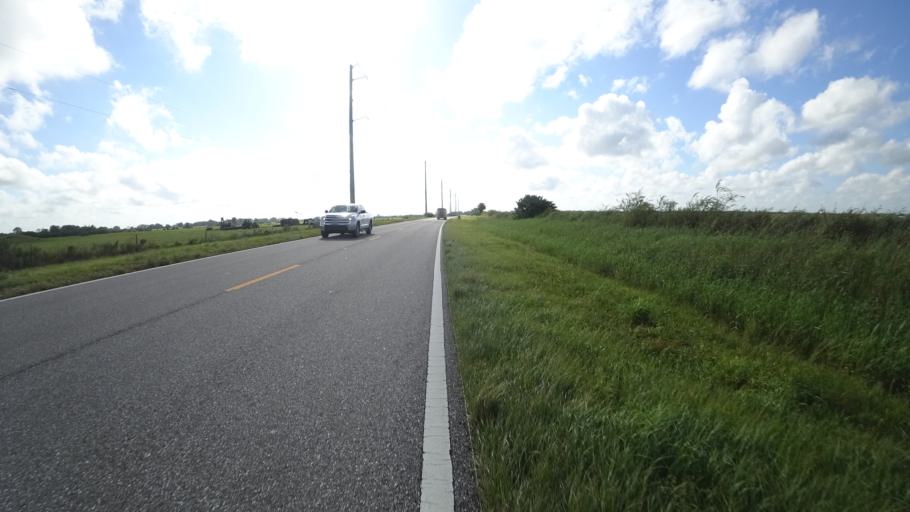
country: US
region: Florida
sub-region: Hillsborough County
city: Wimauma
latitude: 27.5203
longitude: -82.3284
